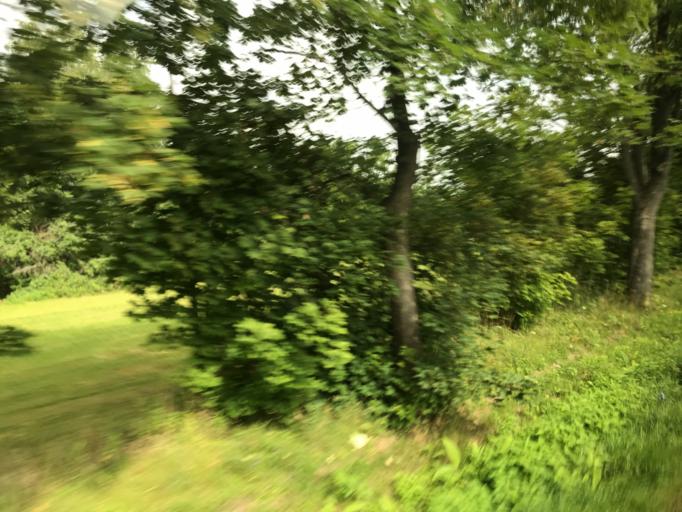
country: CZ
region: Jihocesky
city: Vcelna
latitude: 48.9359
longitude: 14.4634
